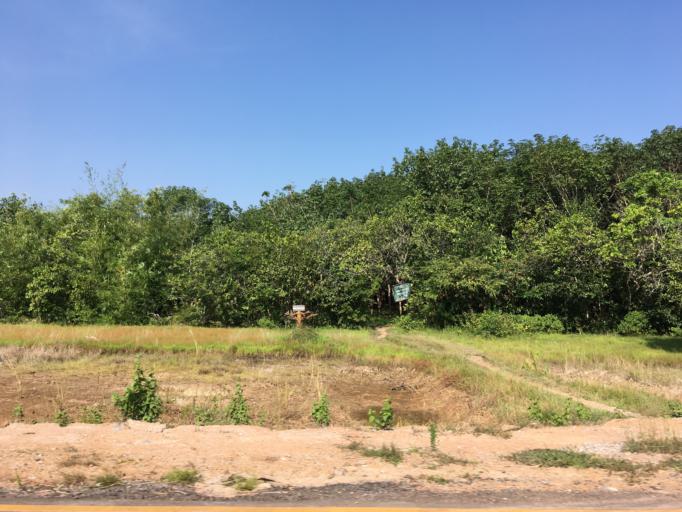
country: MM
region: Mon
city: Martaban
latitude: 16.6526
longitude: 97.7408
